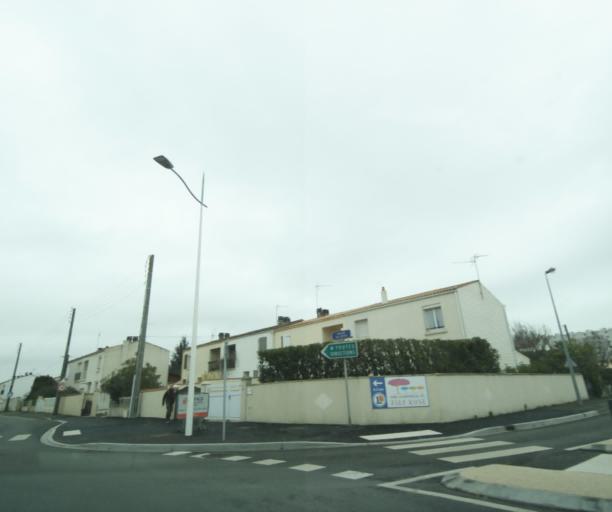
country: FR
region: Poitou-Charentes
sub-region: Departement de la Charente-Maritime
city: La Rochelle
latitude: 46.1721
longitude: -1.1769
